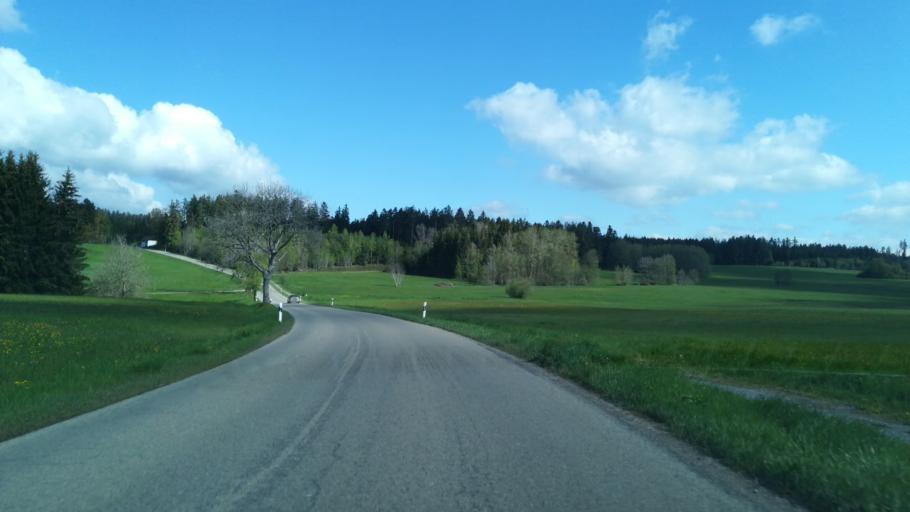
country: DE
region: Baden-Wuerttemberg
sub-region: Freiburg Region
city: Grafenhausen
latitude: 47.7545
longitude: 8.3038
